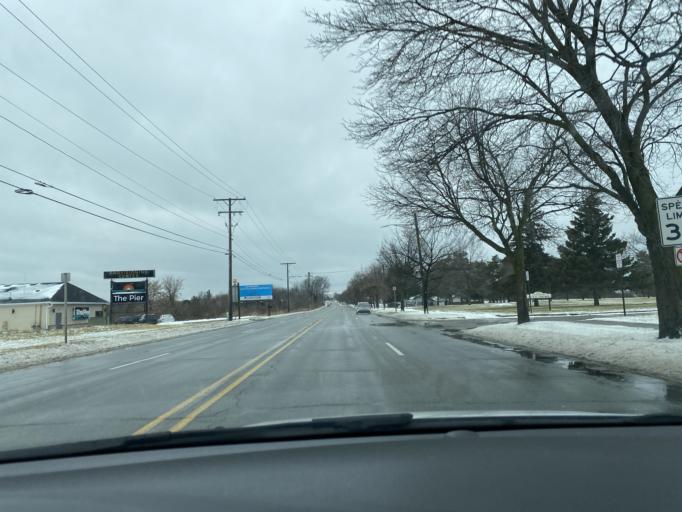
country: US
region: Michigan
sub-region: Lapeer County
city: Lapeer
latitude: 43.0504
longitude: -83.3321
